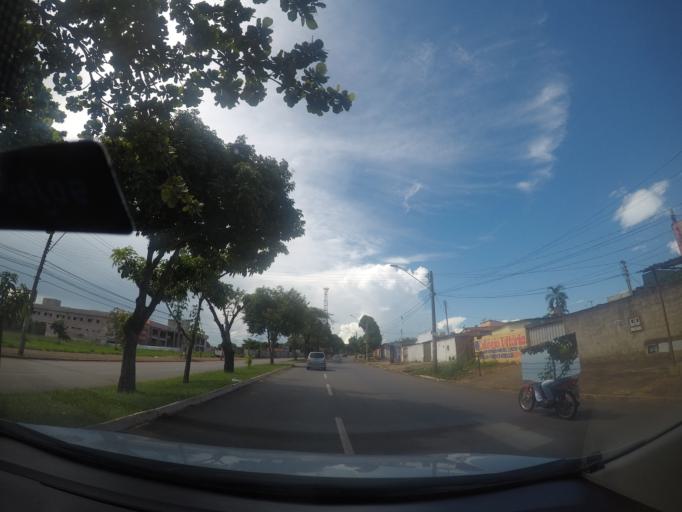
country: BR
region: Goias
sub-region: Trindade
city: Trindade
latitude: -16.6644
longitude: -49.3870
